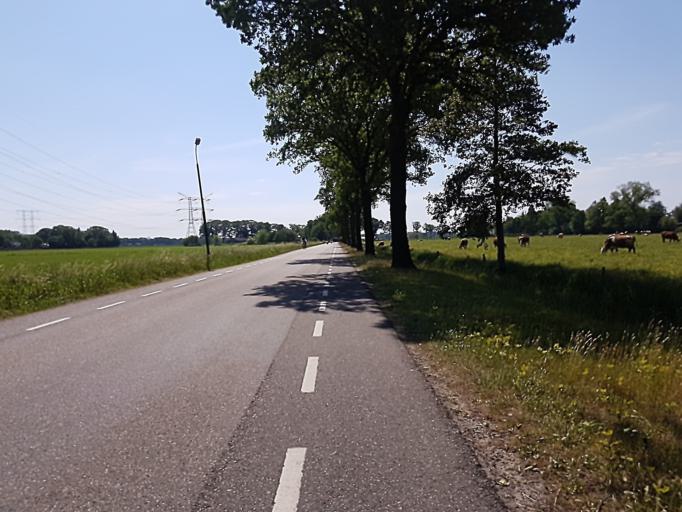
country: NL
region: North Brabant
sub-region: Gemeente Dongen
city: Dongen
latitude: 51.6271
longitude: 4.9973
